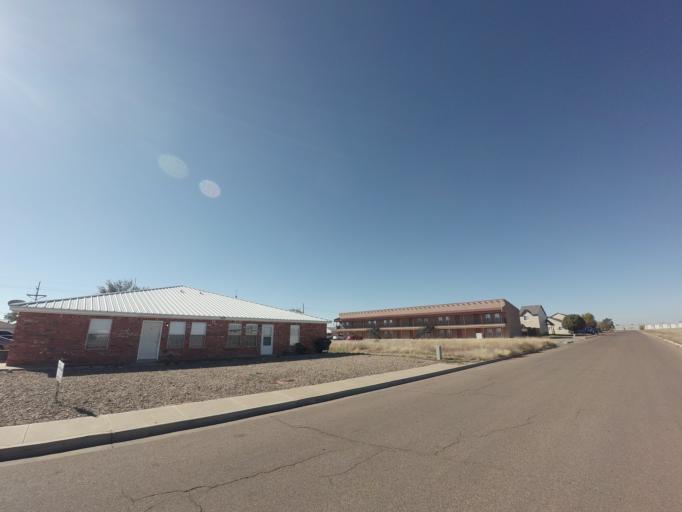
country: US
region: New Mexico
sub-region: Curry County
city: Clovis
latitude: 34.4311
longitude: -103.2054
